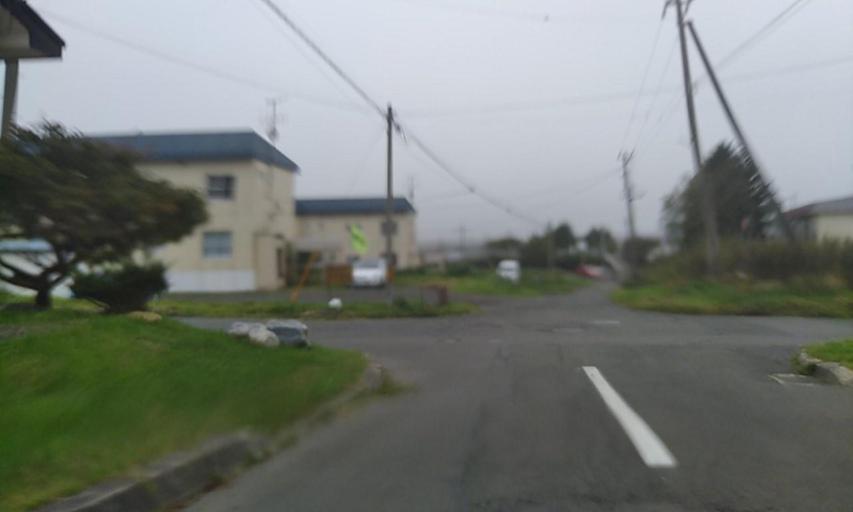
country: JP
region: Hokkaido
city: Nemuro
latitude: 43.3237
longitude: 145.5986
